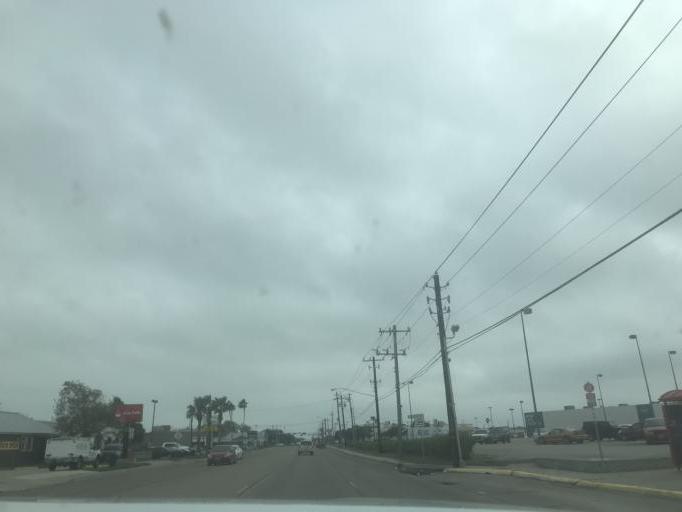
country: US
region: Texas
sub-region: Nueces County
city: Corpus Christi
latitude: 27.7097
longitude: -97.3656
